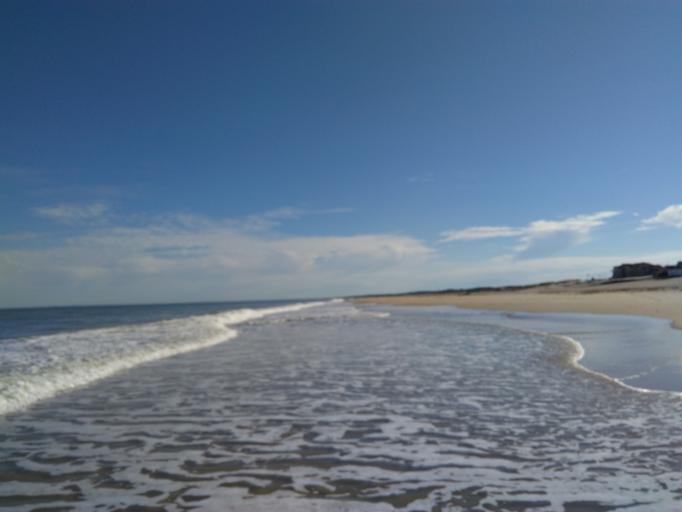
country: FR
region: Aquitaine
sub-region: Departement de la Gironde
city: Soulac-sur-Mer
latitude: 45.5151
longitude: -1.1310
